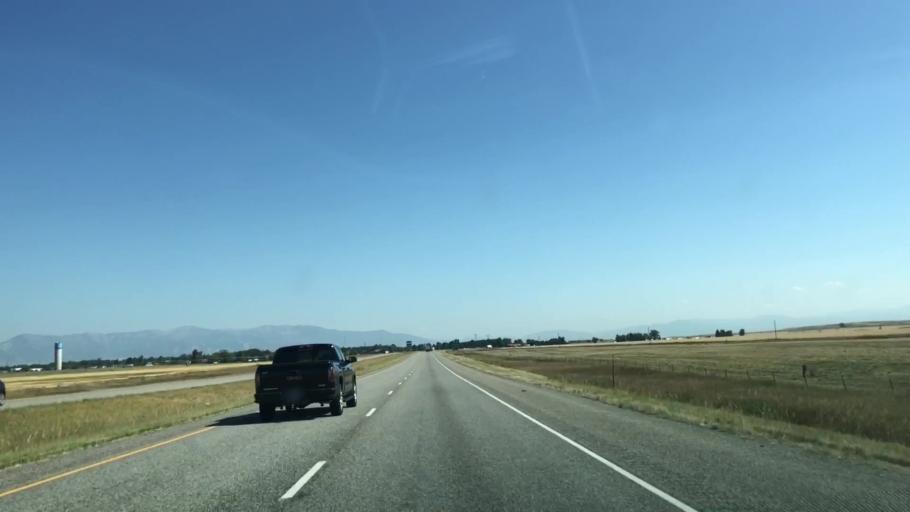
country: US
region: Montana
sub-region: Gallatin County
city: Manhattan
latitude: 45.8631
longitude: -111.3631
